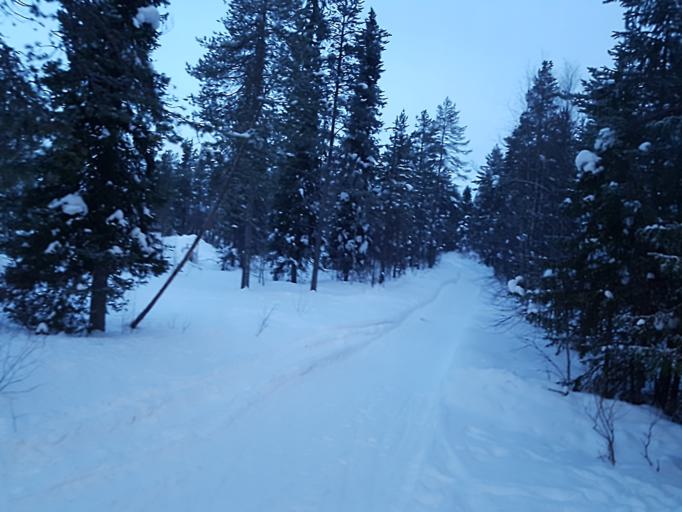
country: FI
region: Lapland
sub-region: Tunturi-Lappi
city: Kolari
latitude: 67.6176
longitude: 24.1413
